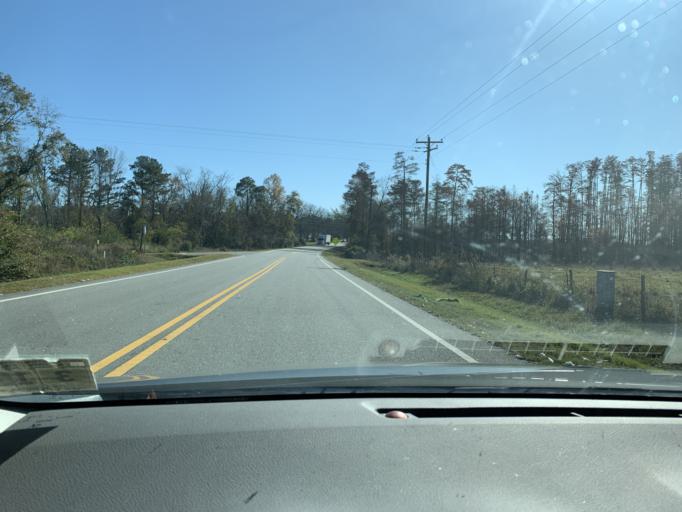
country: US
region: Georgia
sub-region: Ben Hill County
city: Fitzgerald
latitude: 31.7128
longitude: -83.1709
